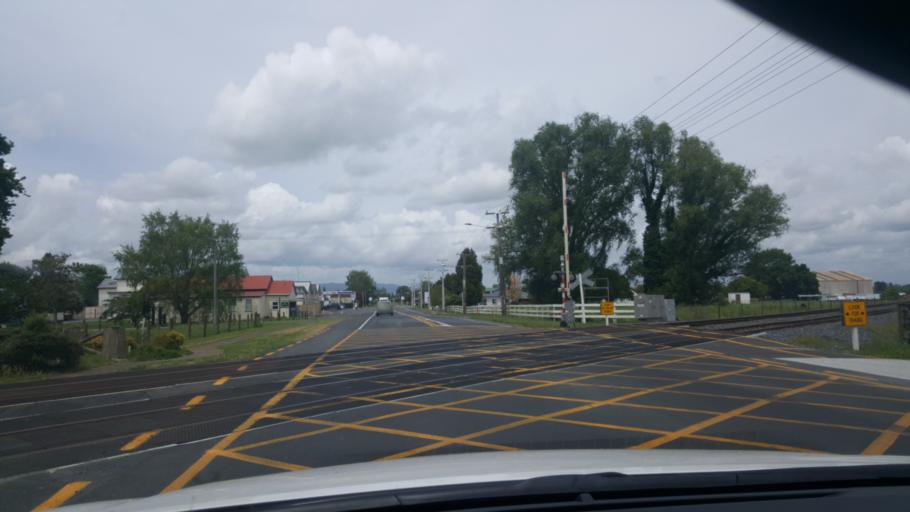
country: NZ
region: Waikato
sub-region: Matamata-Piako District
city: Matamata
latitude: -37.8820
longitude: 175.7598
